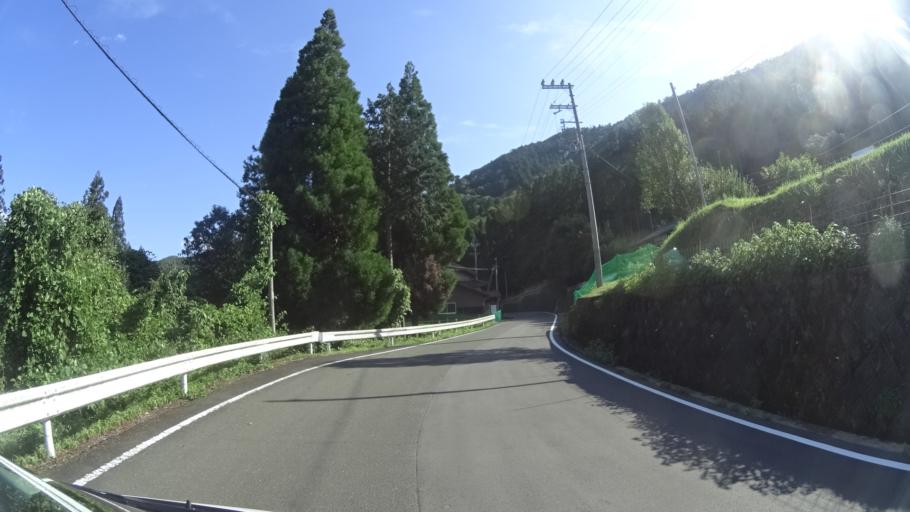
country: JP
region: Kyoto
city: Ayabe
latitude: 35.2789
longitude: 135.3309
